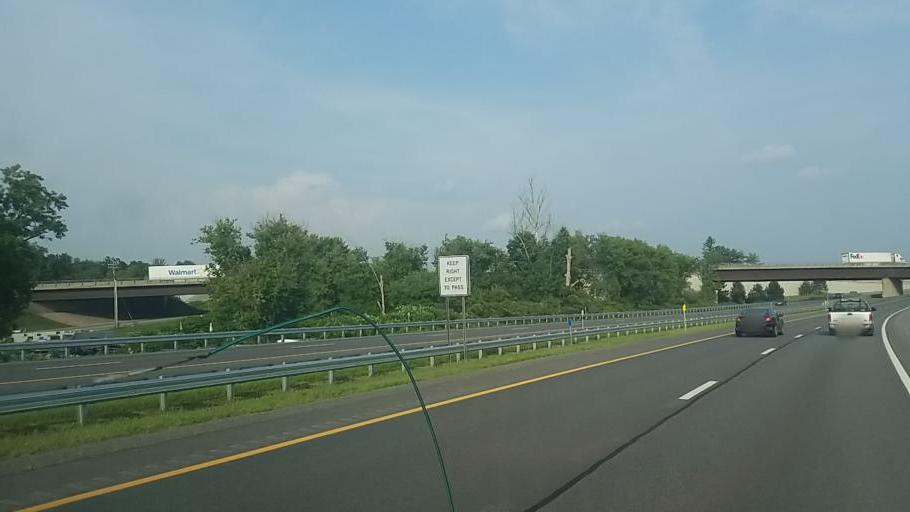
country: US
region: New York
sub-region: Oneida County
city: Whitesboro
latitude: 43.1371
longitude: -75.2733
